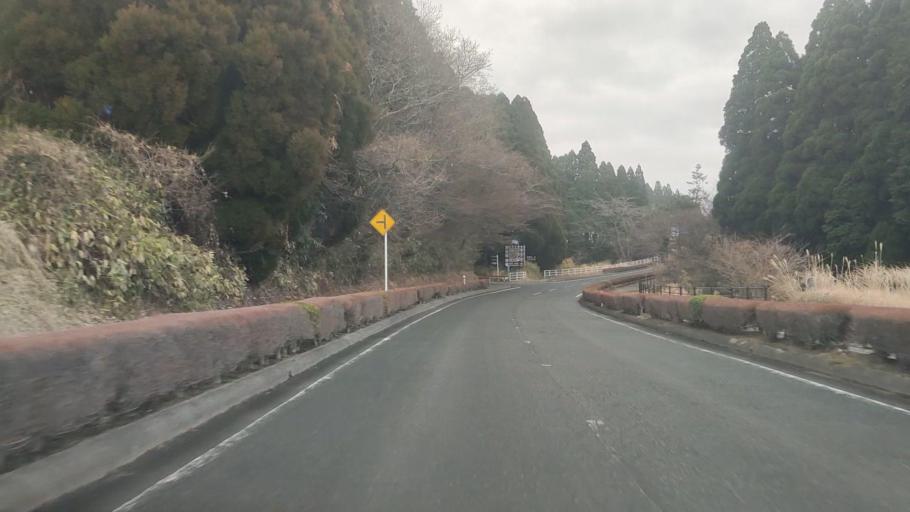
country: JP
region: Kumamoto
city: Aso
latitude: 32.8336
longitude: 131.0721
